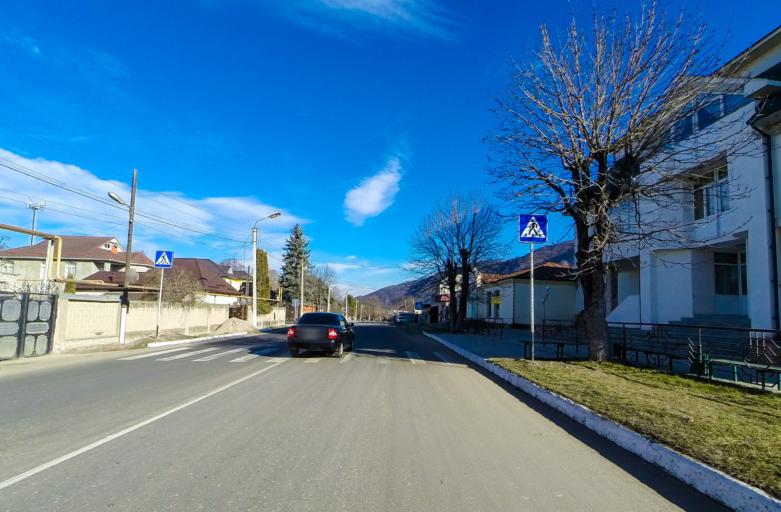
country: RU
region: Kabardino-Balkariya
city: Belaya Rechka
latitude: 43.4400
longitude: 43.5809
